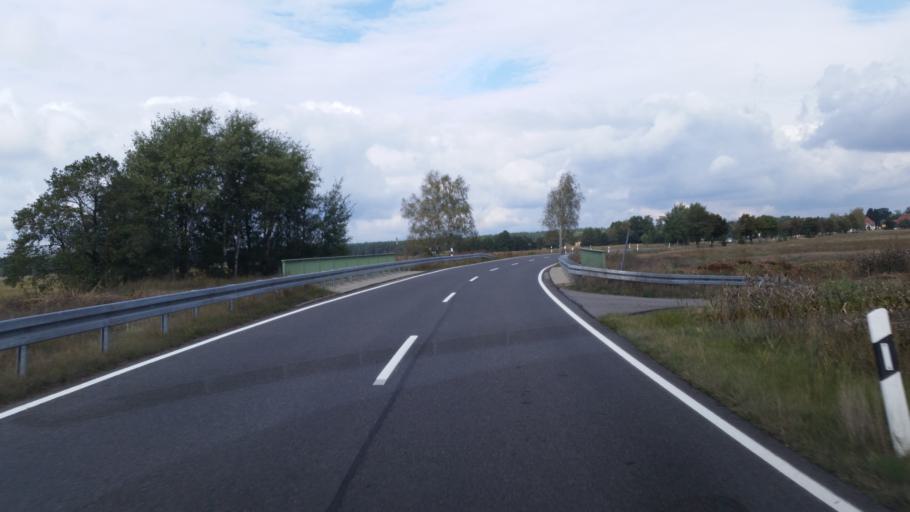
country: DE
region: Brandenburg
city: Grunewald
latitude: 51.3929
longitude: 13.9878
